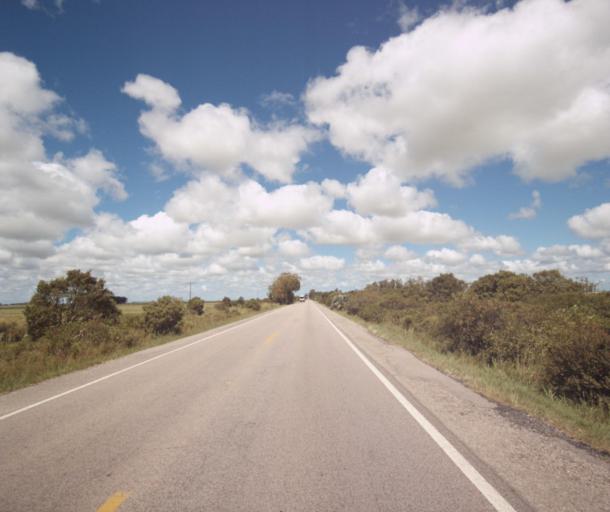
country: BR
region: Rio Grande do Sul
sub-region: Rio Grande
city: Rio Grande
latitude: -32.1795
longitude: -52.4219
